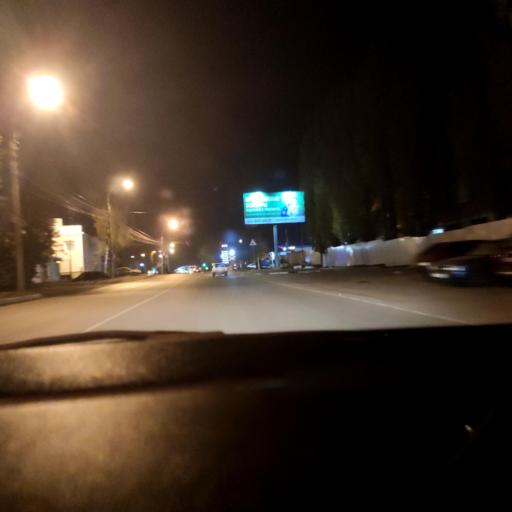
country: RU
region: Voronezj
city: Voronezh
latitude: 51.6663
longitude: 39.1503
